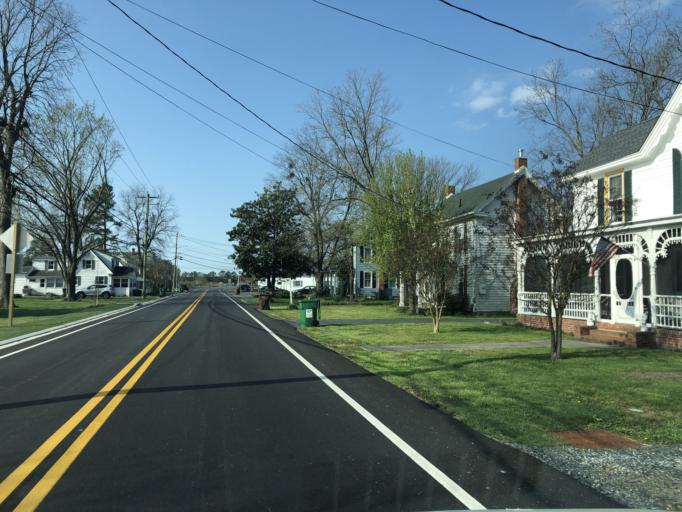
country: US
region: Maryland
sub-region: Dorchester County
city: Algonquin
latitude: 38.5036
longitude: -76.1512
